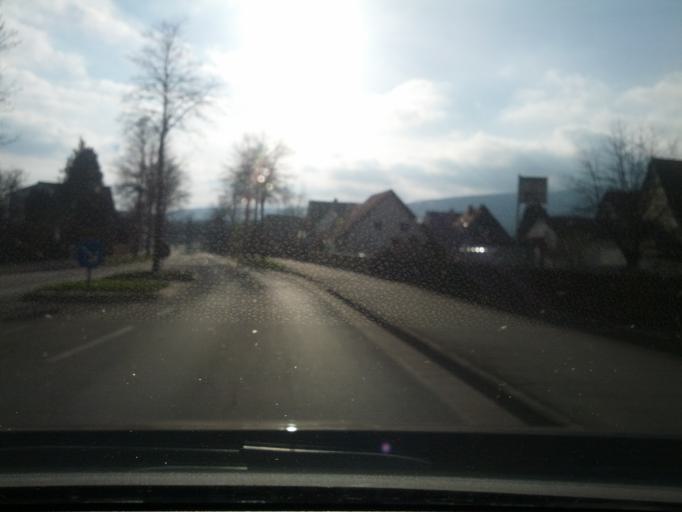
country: DE
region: Lower Saxony
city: Buhren
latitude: 51.4936
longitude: 9.6026
